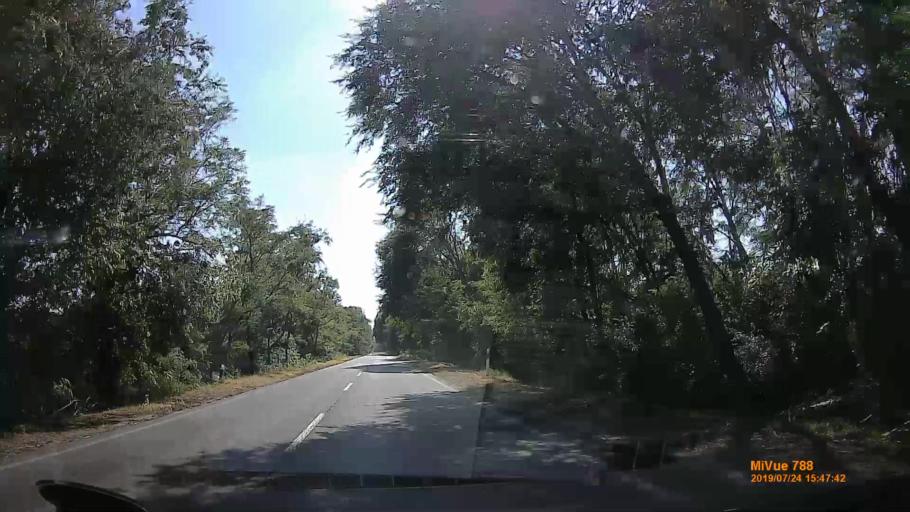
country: HU
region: Szabolcs-Szatmar-Bereg
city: Nyirmada
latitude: 48.0753
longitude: 22.2453
